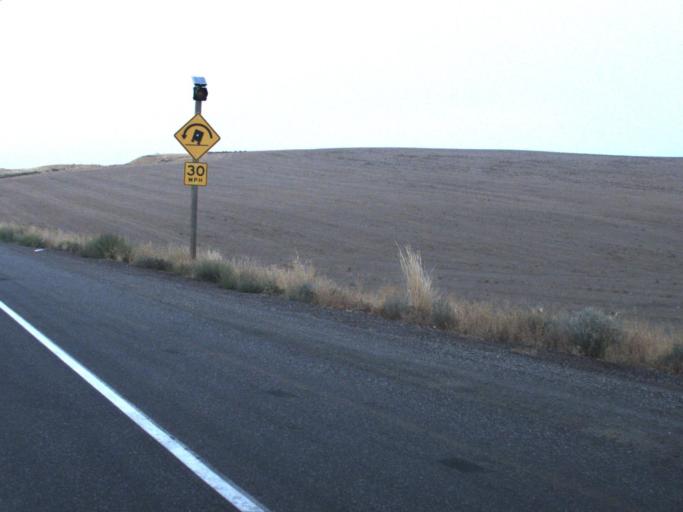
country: US
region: Washington
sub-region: Benton County
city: Prosser
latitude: 46.2038
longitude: -119.7058
